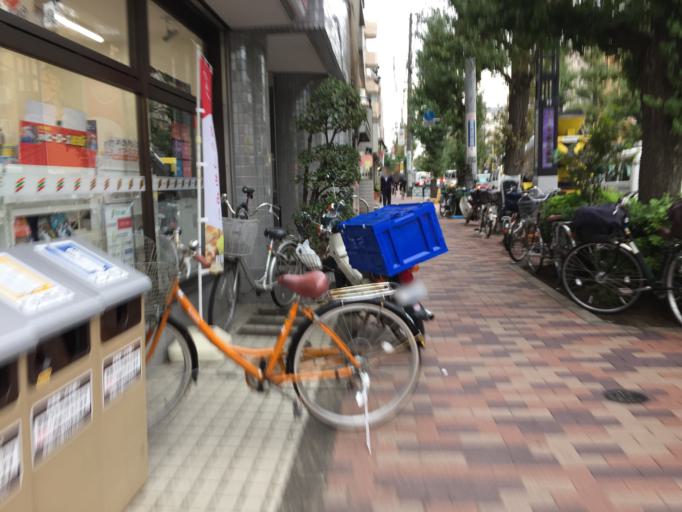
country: JP
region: Tokyo
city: Tokyo
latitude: 35.6423
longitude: 139.6547
